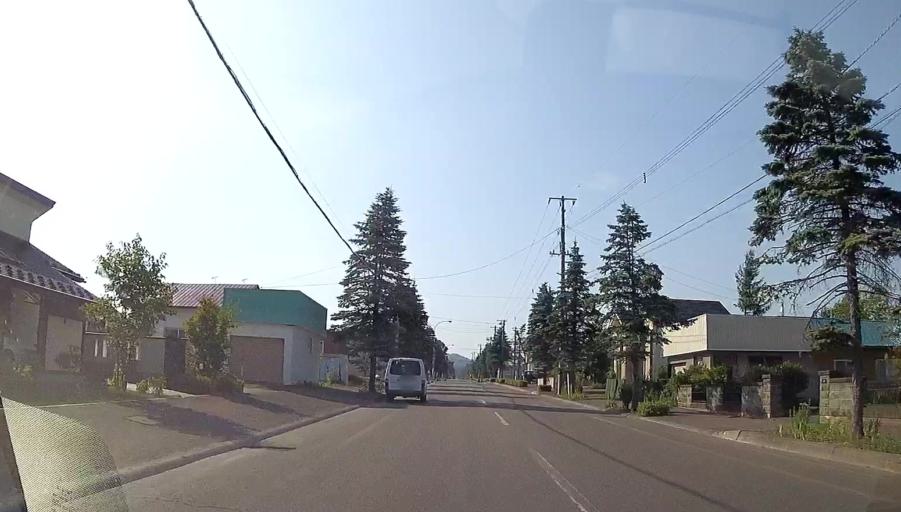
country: JP
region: Hokkaido
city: Otofuke
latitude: 43.0071
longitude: 142.8771
